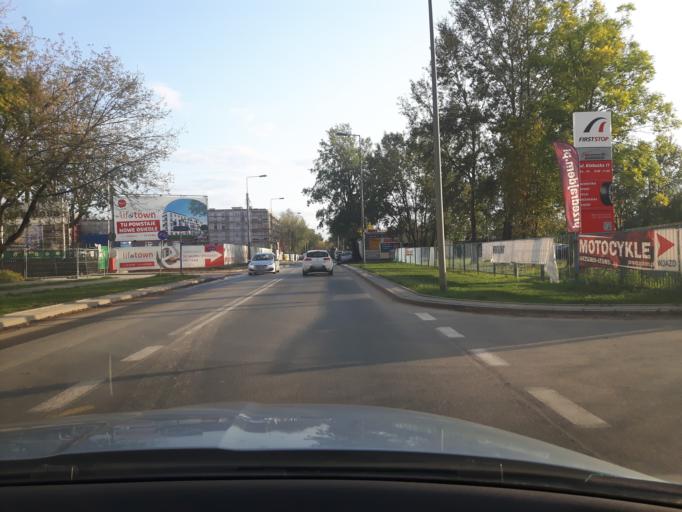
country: PL
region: Masovian Voivodeship
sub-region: Warszawa
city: Wlochy
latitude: 52.1621
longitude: 20.9923
